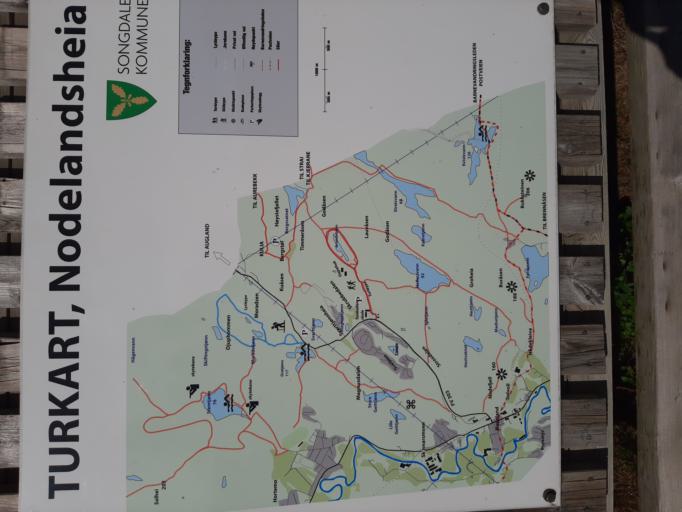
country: NO
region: Vest-Agder
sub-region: Songdalen
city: Nodeland
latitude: 58.1674
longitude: 7.8586
